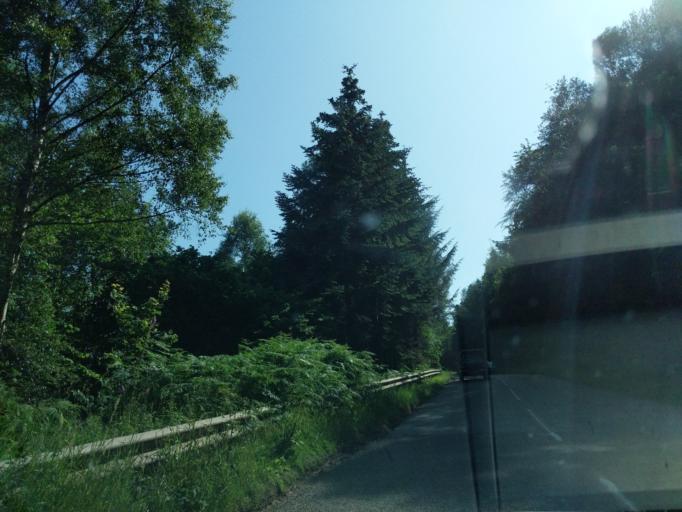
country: GB
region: Scotland
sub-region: Moray
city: Rothes
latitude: 57.4937
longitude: -3.1919
